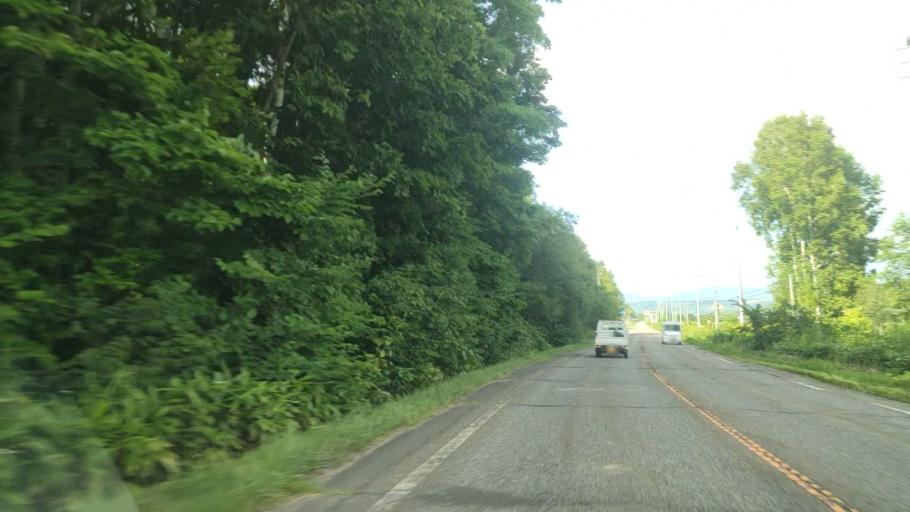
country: JP
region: Hokkaido
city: Nayoro
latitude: 44.3957
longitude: 142.3940
